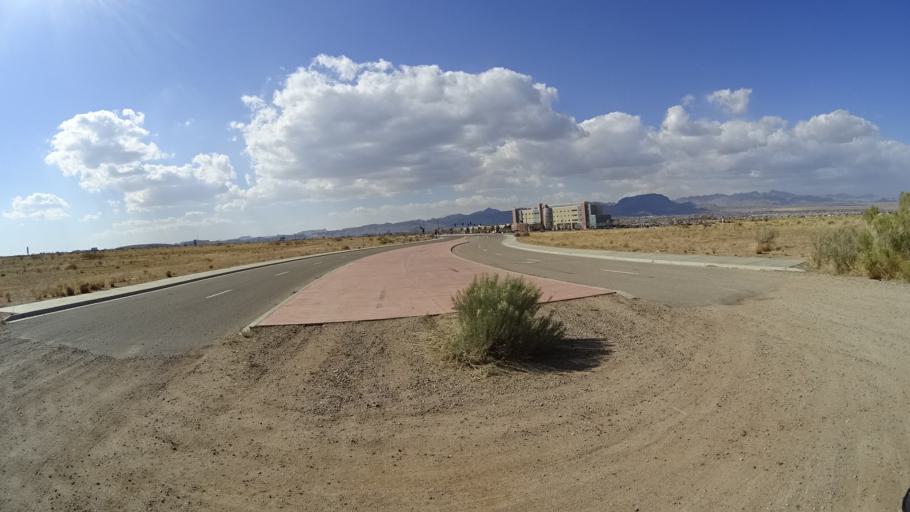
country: US
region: Arizona
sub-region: Mohave County
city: New Kingman-Butler
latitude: 35.2174
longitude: -113.9813
